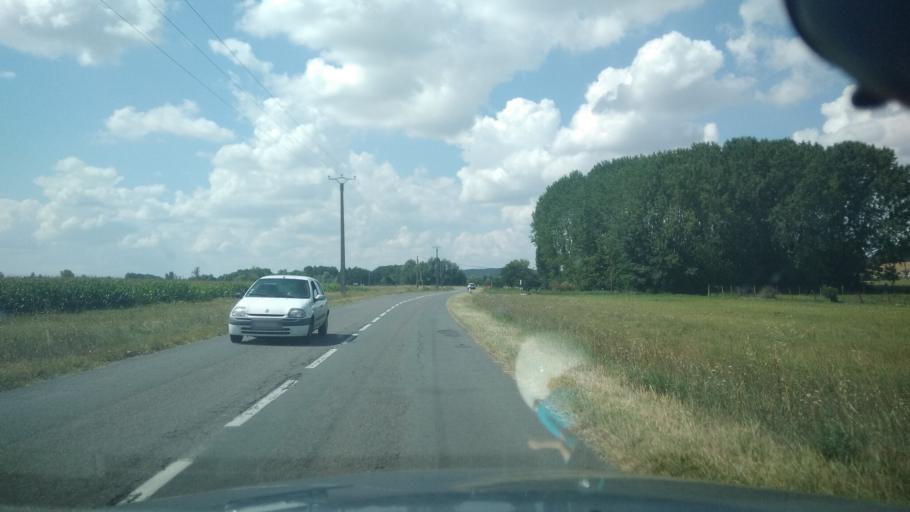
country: FR
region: Poitou-Charentes
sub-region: Departement de la Vienne
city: Dange-Saint-Romain
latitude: 46.9292
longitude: 0.5921
